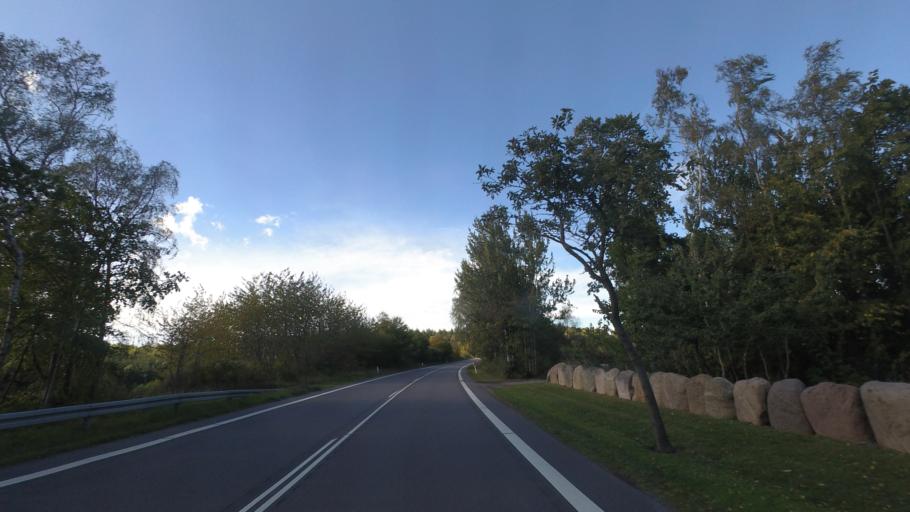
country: DK
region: Capital Region
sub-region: Bornholm Kommune
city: Ronne
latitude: 55.0801
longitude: 14.7570
